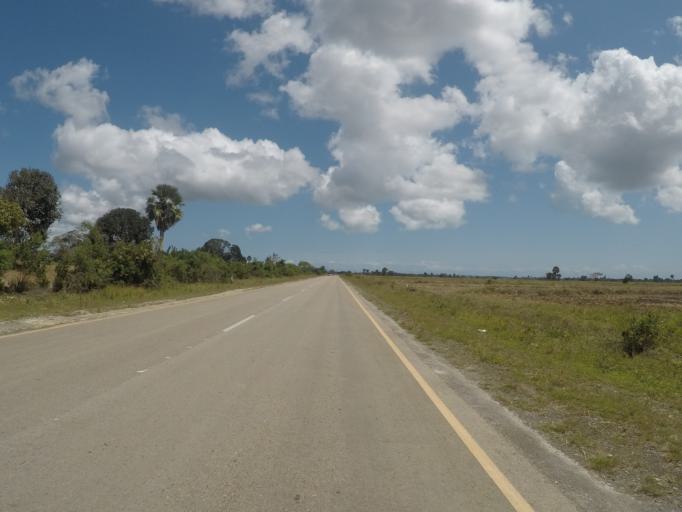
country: TZ
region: Zanzibar Central/South
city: Koani
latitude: -6.2033
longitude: 39.3682
